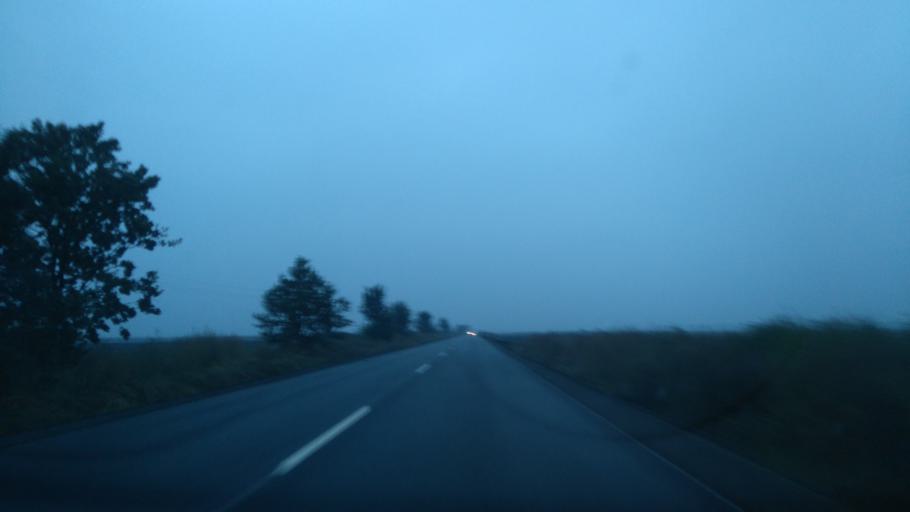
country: RS
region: Autonomna Pokrajina Vojvodina
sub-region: Juznobacki Okrug
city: Becej
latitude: 45.6637
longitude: 20.0507
